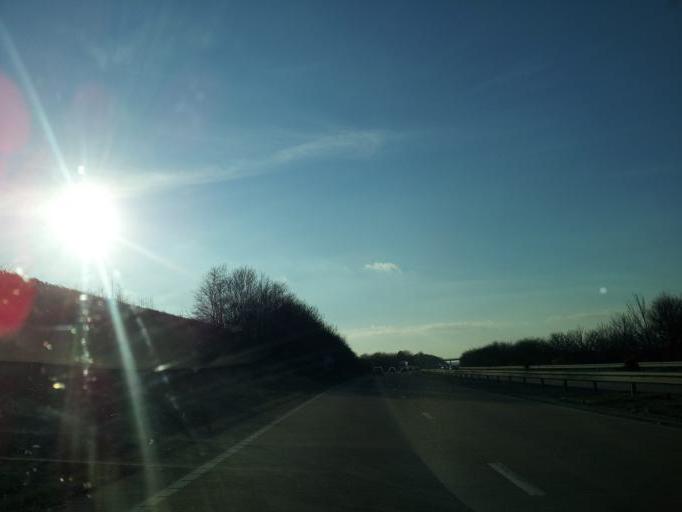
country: GB
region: England
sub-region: Devon
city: Okehampton
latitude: 50.7306
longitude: -3.8750
